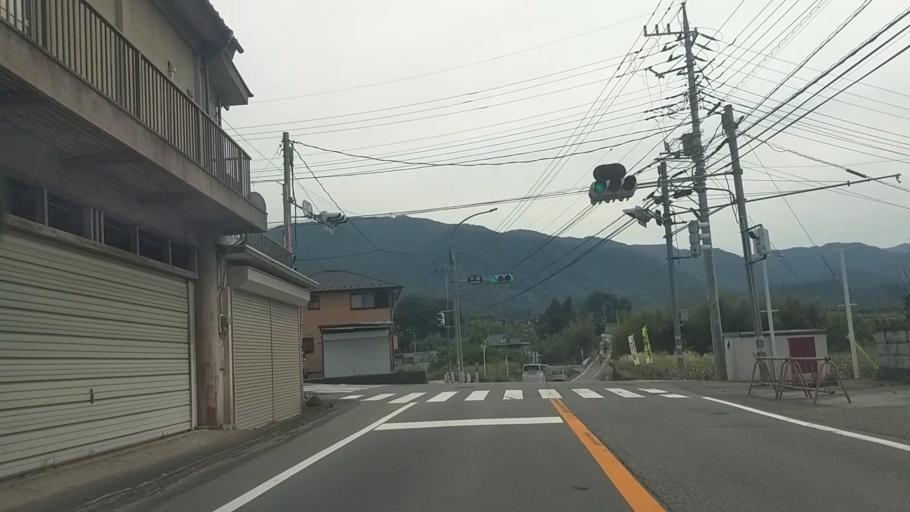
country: JP
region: Yamanashi
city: Isawa
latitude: 35.5773
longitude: 138.5931
